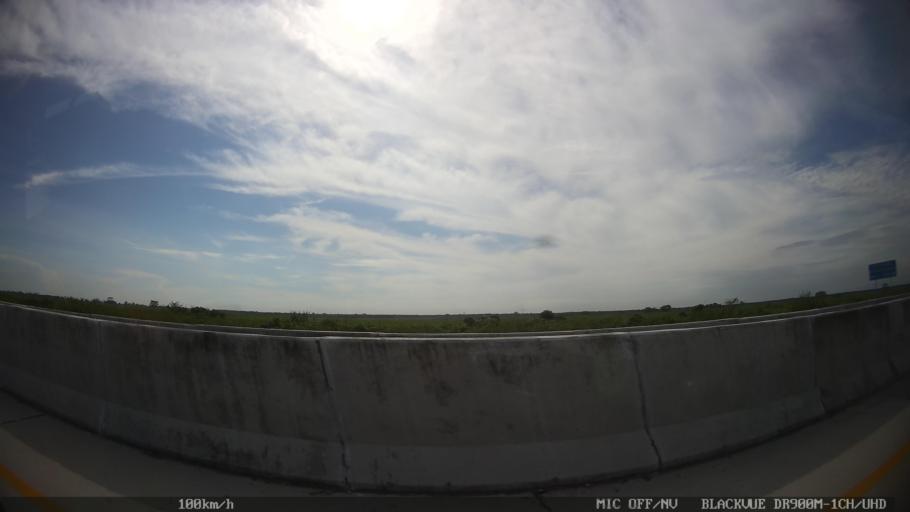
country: ID
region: North Sumatra
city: Binjai
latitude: 3.6769
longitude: 98.5361
